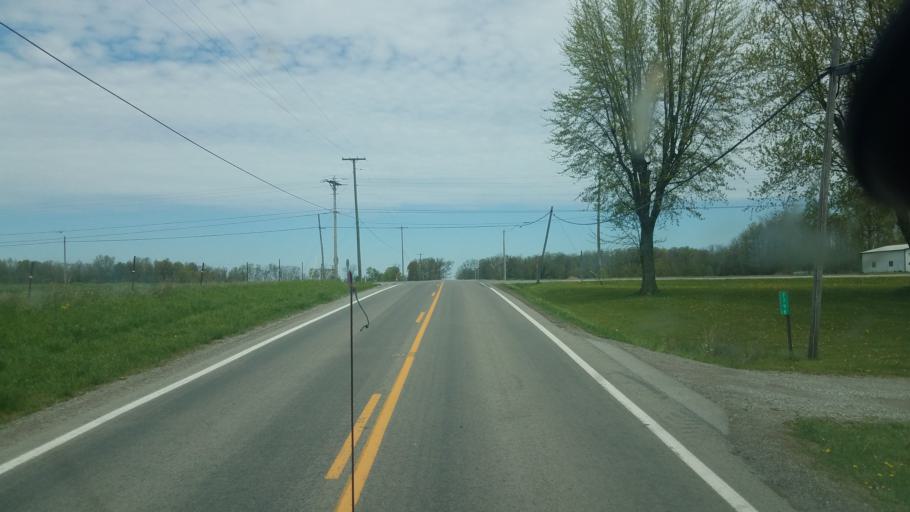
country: US
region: Ohio
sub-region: Hardin County
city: Ada
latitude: 40.7067
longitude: -83.7851
